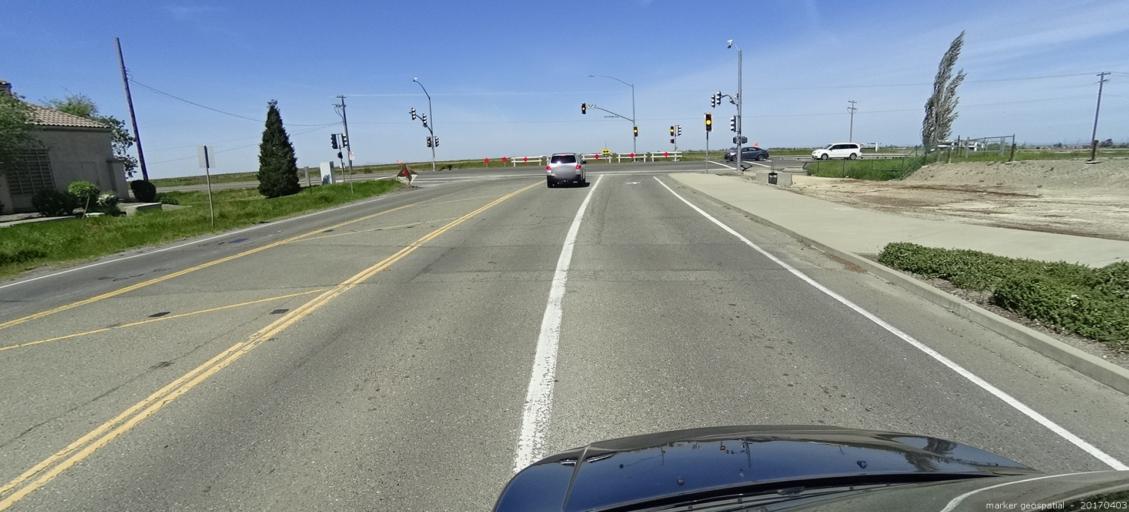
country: US
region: California
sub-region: Sacramento County
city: Elverta
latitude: 38.6846
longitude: -121.5080
